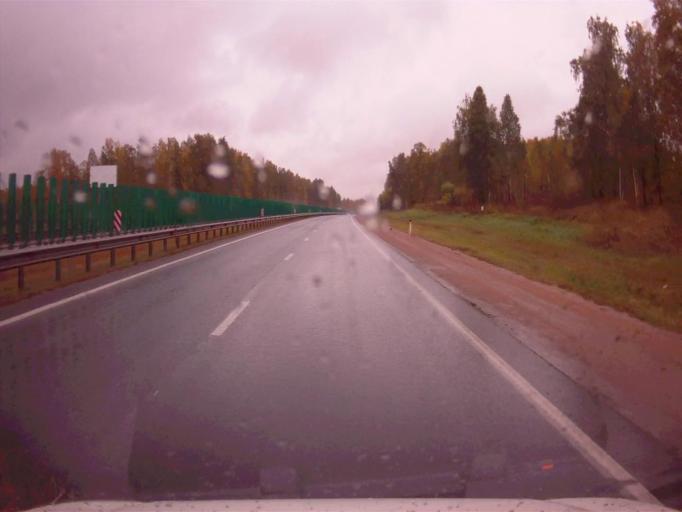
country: RU
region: Chelyabinsk
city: Dolgoderevenskoye
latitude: 55.3329
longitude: 61.3160
